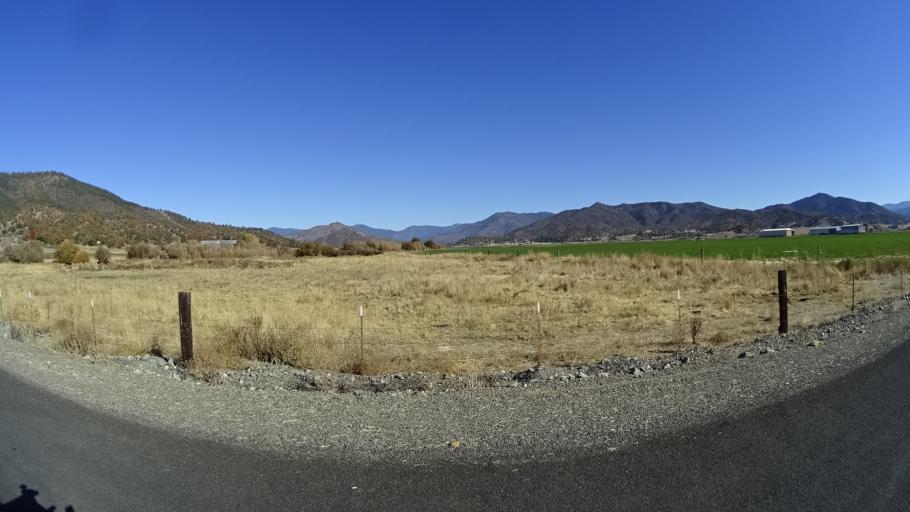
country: US
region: California
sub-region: Siskiyou County
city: Yreka
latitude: 41.5757
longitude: -122.8586
